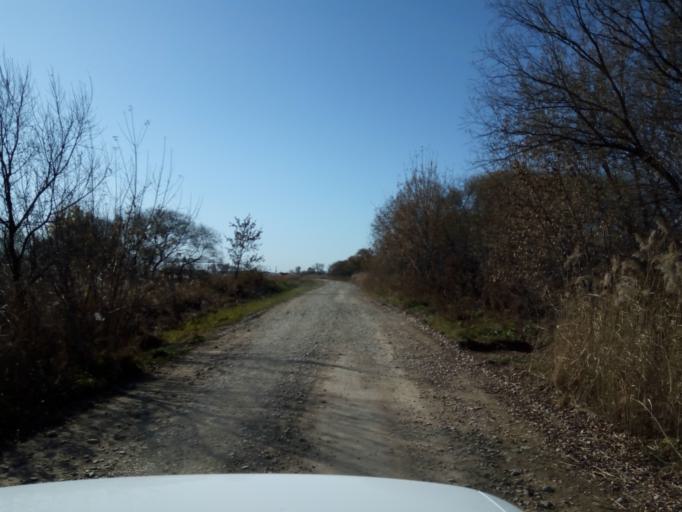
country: RU
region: Primorskiy
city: Dal'nerechensk
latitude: 45.9083
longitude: 133.7965
